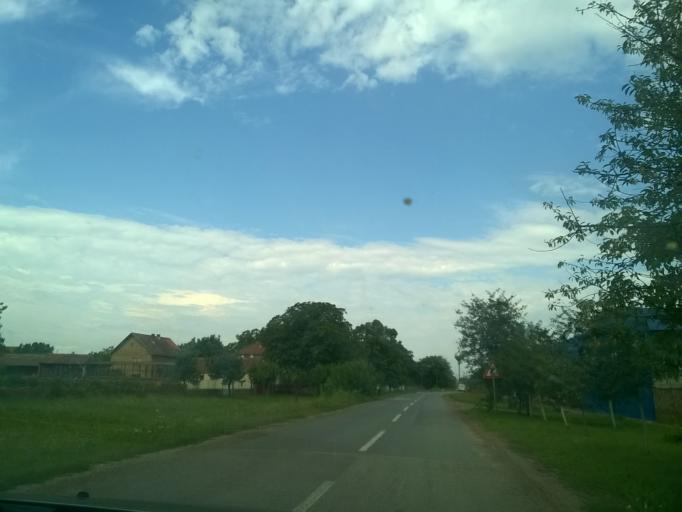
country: RS
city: Orlovat
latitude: 45.2480
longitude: 20.5846
